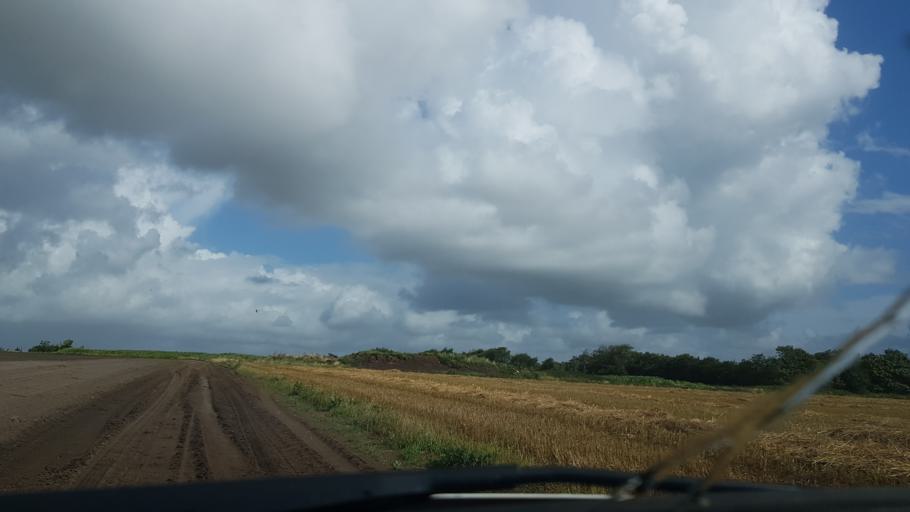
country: DK
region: South Denmark
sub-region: Esbjerg Kommune
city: Ribe
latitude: 55.2567
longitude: 8.7610
